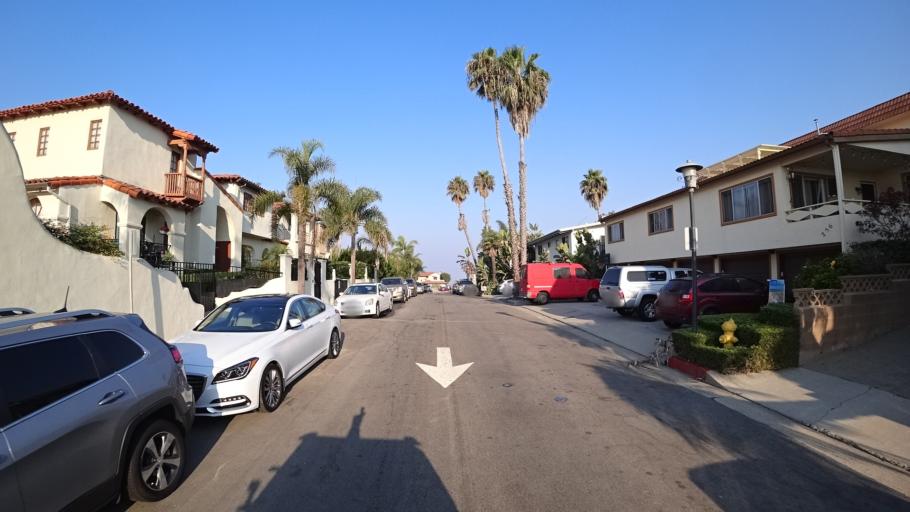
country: US
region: California
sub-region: Orange County
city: San Clemente
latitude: 33.4068
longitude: -117.6065
